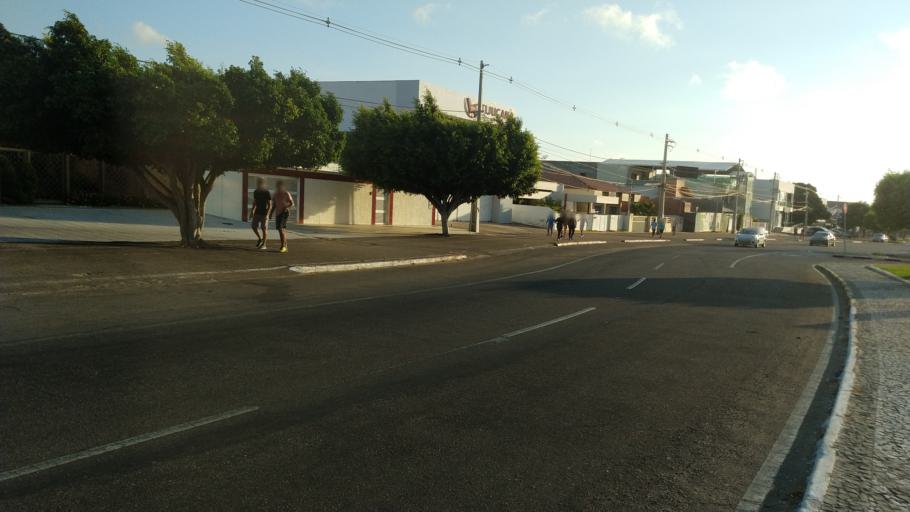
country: BR
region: Bahia
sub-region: Paulo Afonso
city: Paulo Afonso
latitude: -9.3984
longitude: -38.2248
